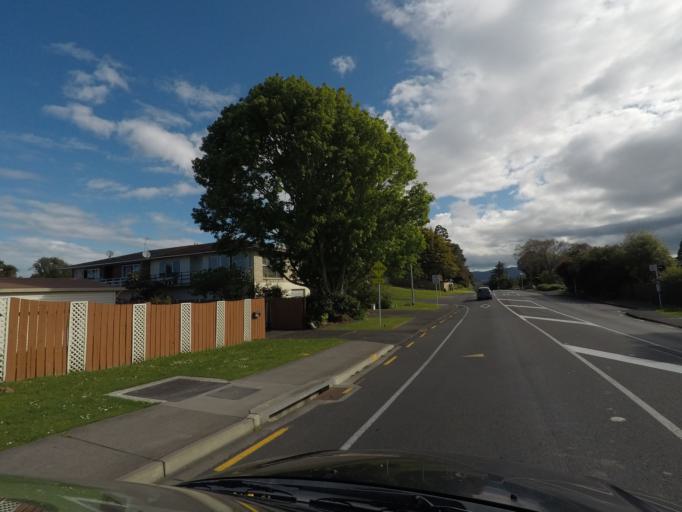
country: NZ
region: Auckland
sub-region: Auckland
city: Rosebank
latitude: -36.8662
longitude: 174.6425
